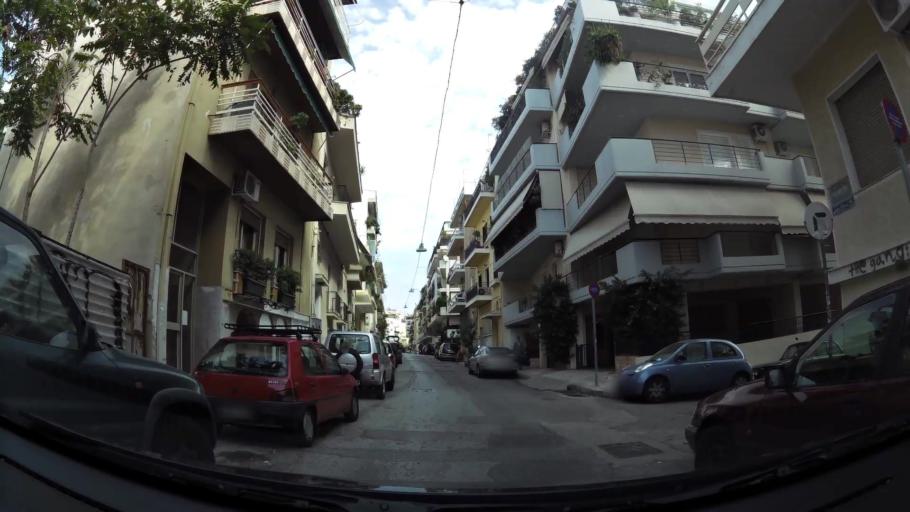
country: GR
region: Attica
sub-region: Nomarchia Athinas
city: Athens
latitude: 37.9656
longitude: 23.7238
